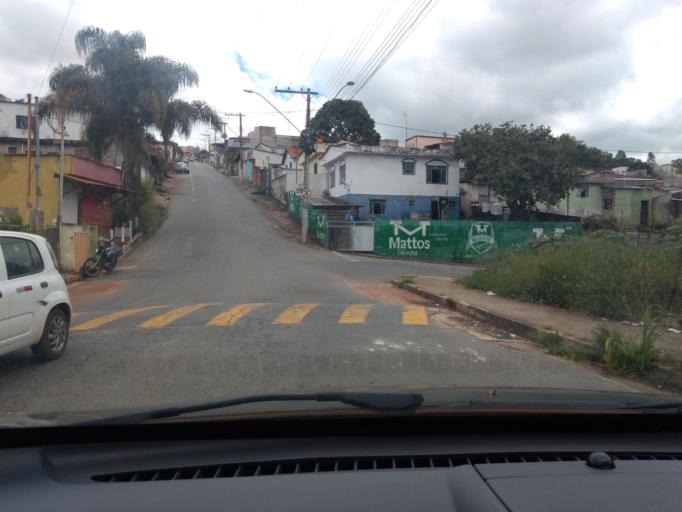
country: BR
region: Minas Gerais
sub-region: Lavras
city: Lavras
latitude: -21.2431
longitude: -45.0108
